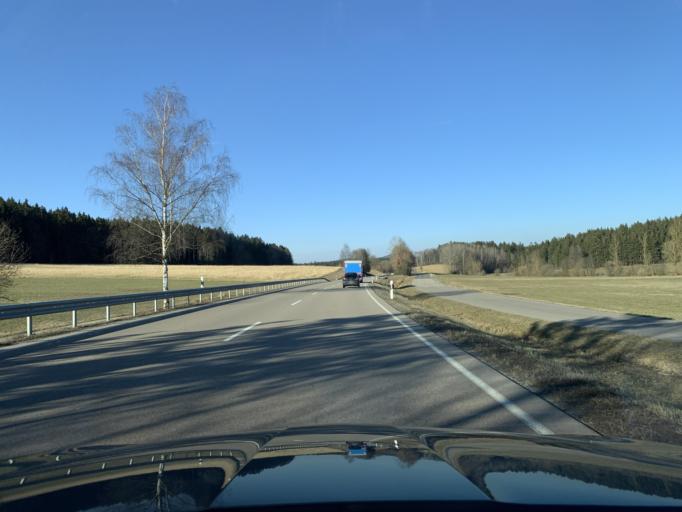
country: DE
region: Bavaria
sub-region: Upper Palatinate
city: Schonthal
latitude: 49.3140
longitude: 12.6311
